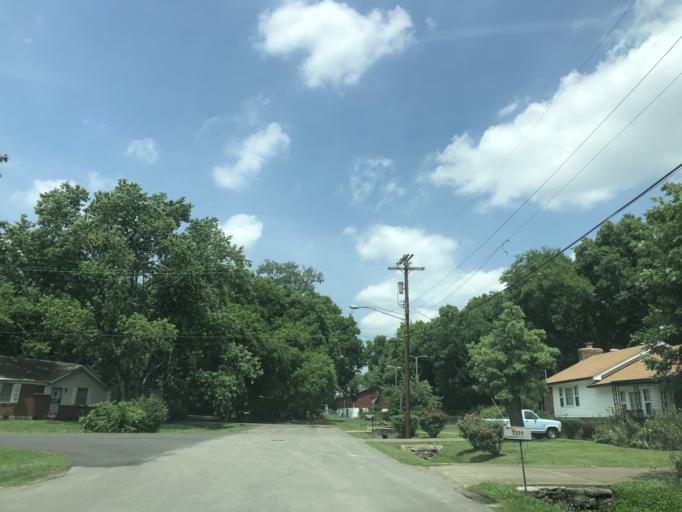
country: US
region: Tennessee
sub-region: Davidson County
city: Nashville
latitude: 36.1958
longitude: -86.7608
